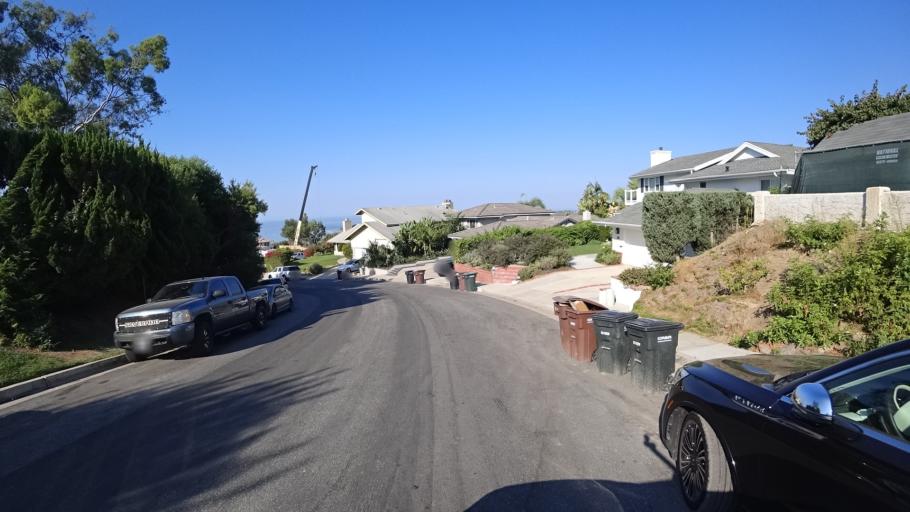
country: US
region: California
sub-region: Orange County
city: San Juan Capistrano
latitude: 33.4675
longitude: -117.6571
